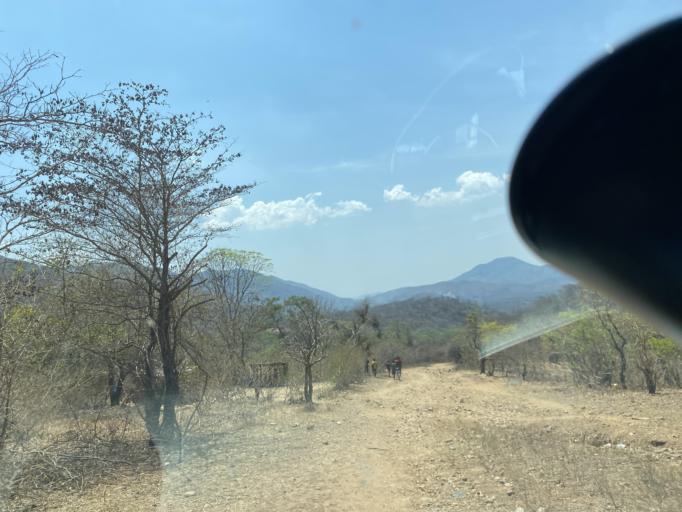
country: ZM
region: Lusaka
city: Kafue
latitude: -15.7948
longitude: 28.4562
